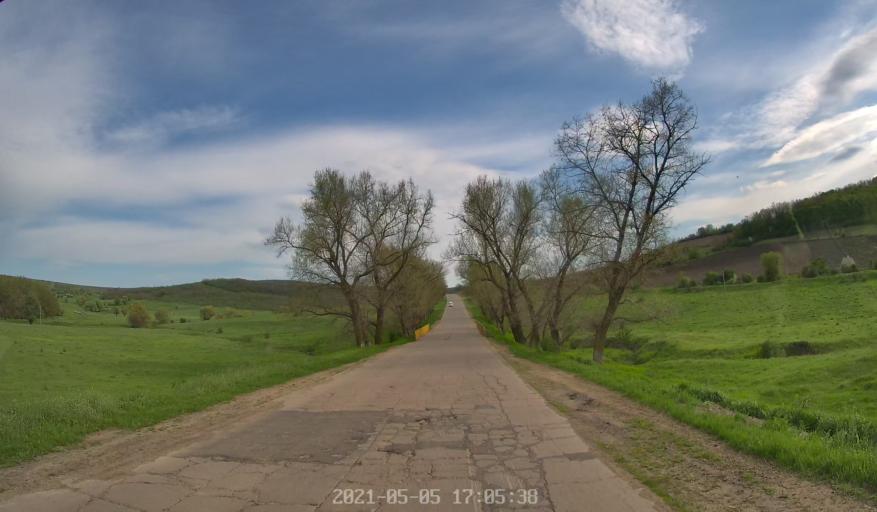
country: MD
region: Chisinau
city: Vadul lui Voda
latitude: 47.0280
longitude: 29.1391
